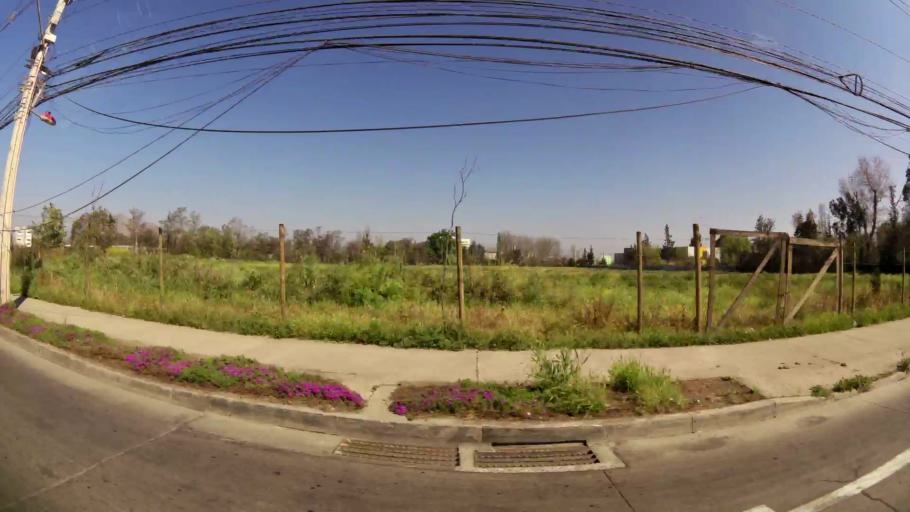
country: CL
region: Santiago Metropolitan
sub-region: Provincia de Chacabuco
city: Chicureo Abajo
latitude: -33.3674
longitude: -70.6707
